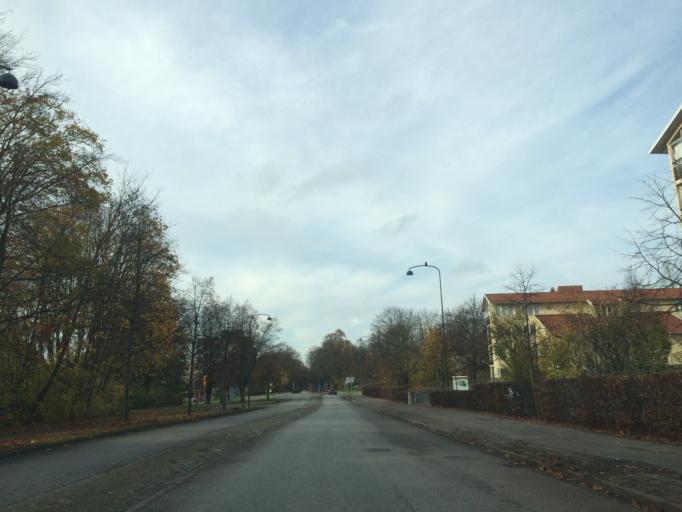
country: SE
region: Skane
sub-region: Lunds Kommun
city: Lund
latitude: 55.6999
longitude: 13.2093
